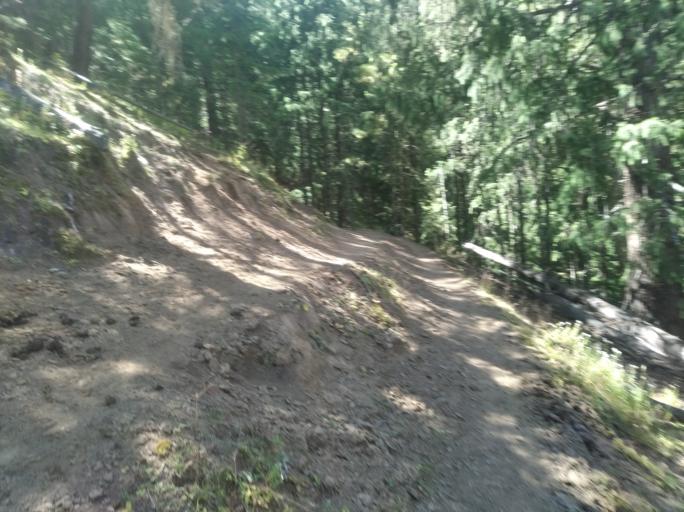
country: NP
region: Western Region
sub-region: Dhawalagiri Zone
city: Jomsom
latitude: 28.8850
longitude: 83.0662
